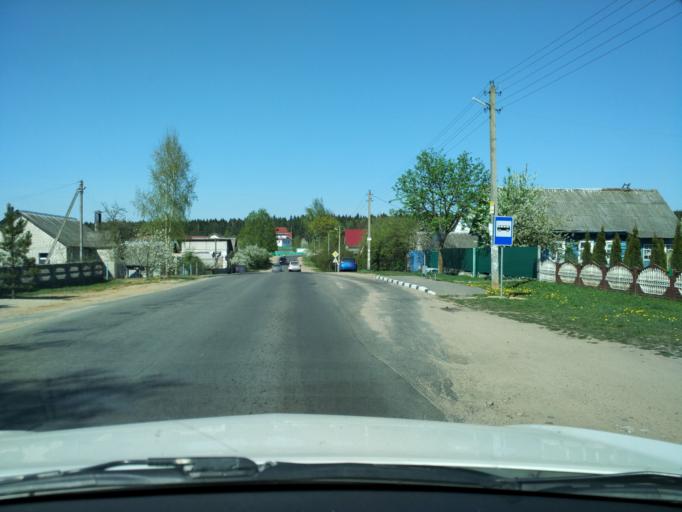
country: BY
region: Minsk
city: Lyeskawka
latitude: 54.0016
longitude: 27.7181
